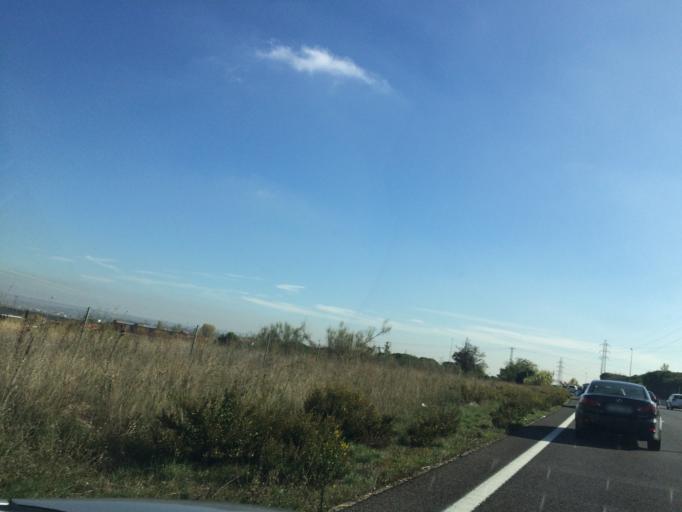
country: ES
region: Madrid
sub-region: Provincia de Madrid
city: Las Tablas
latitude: 40.5419
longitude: -3.7014
